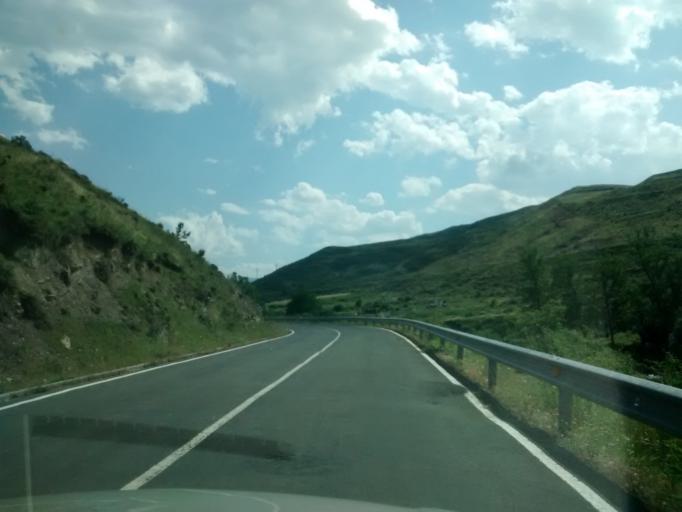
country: ES
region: La Rioja
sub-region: Provincia de La Rioja
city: Jalon de Cameros
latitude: 42.2180
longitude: -2.4776
